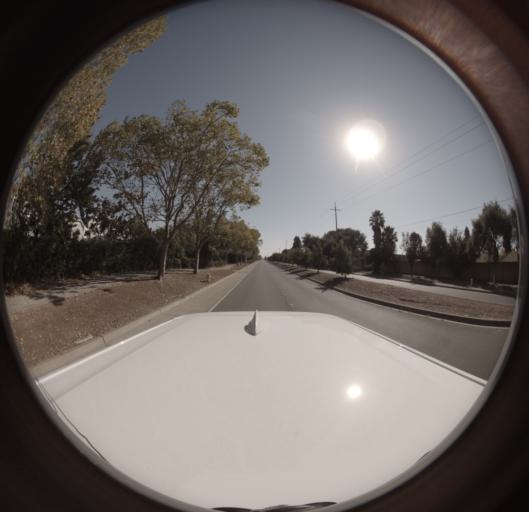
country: US
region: California
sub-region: Sonoma County
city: Petaluma
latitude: 38.2622
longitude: -122.6289
